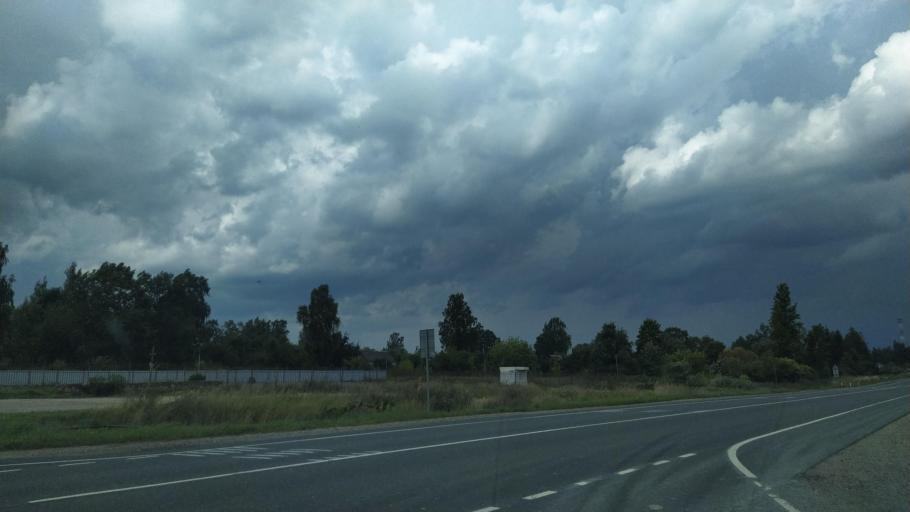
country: RU
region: Pskov
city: Pskov
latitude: 57.5853
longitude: 28.3195
